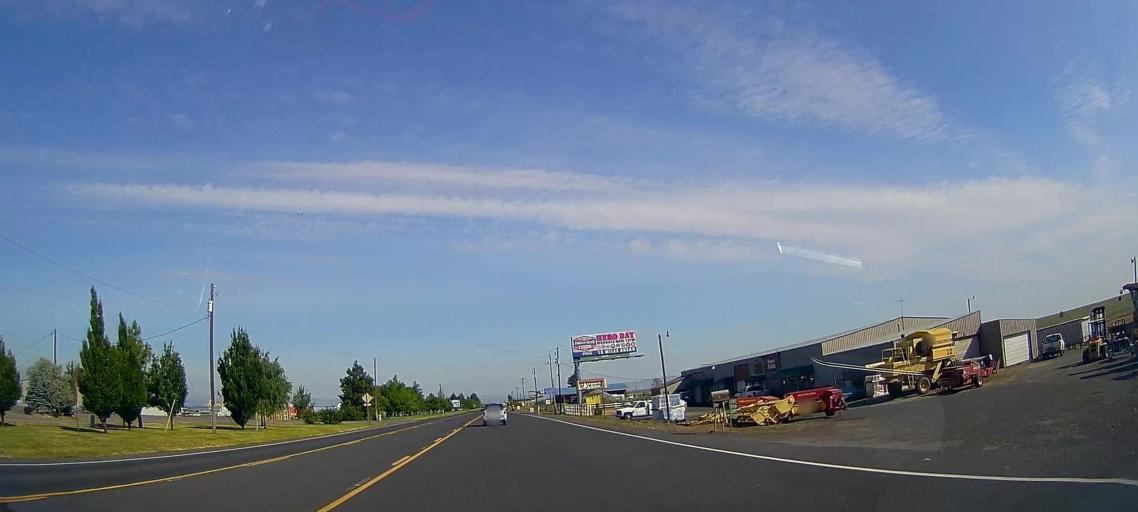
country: US
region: Oregon
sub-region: Jefferson County
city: Madras
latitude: 44.6583
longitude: -121.1313
